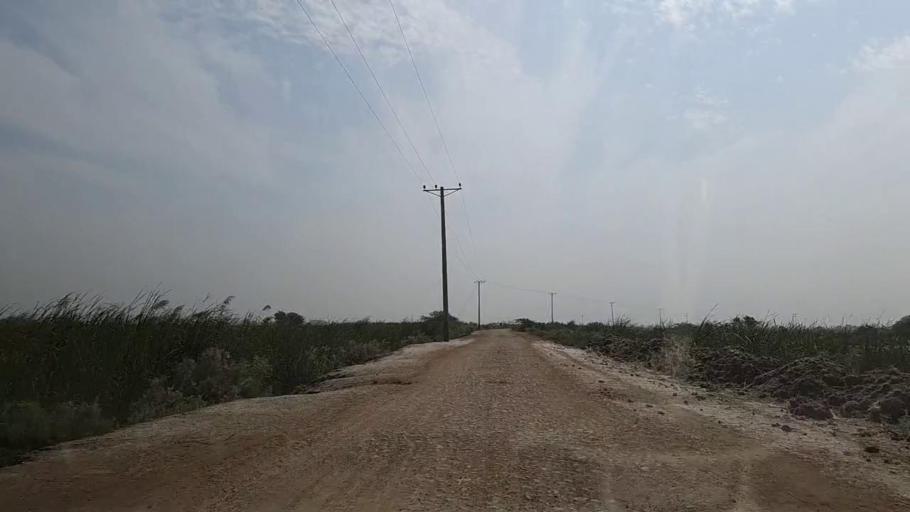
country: PK
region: Sindh
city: Mirpur Batoro
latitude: 24.6013
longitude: 68.2139
